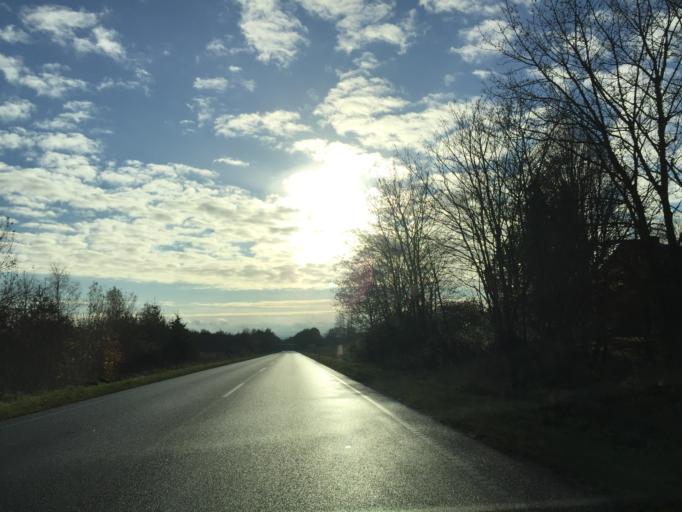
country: DK
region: Central Jutland
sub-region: Arhus Kommune
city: Framlev
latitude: 56.1901
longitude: 10.0069
